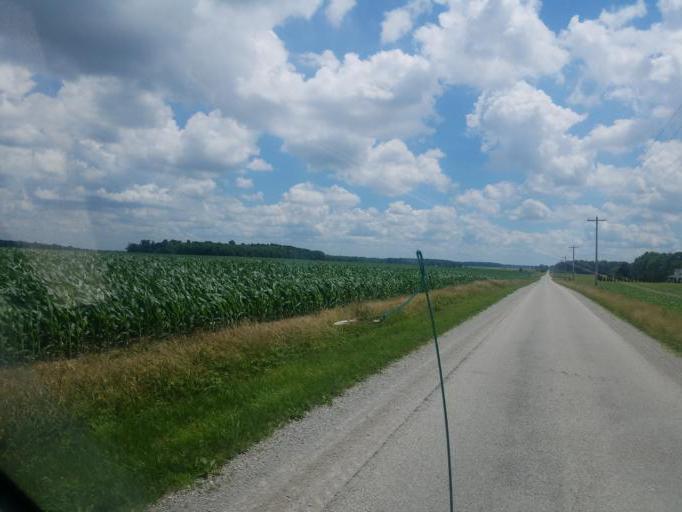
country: US
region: Ohio
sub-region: Huron County
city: Willard
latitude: 41.0438
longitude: -82.8312
